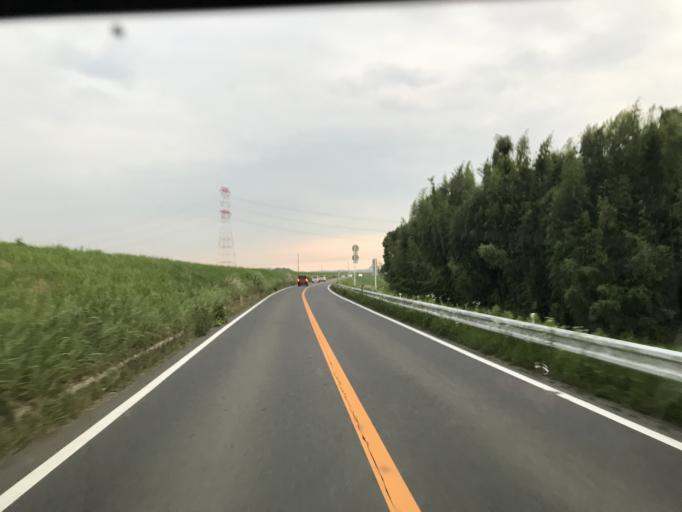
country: JP
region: Ibaraki
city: Fujishiro
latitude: 35.8683
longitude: 140.1216
